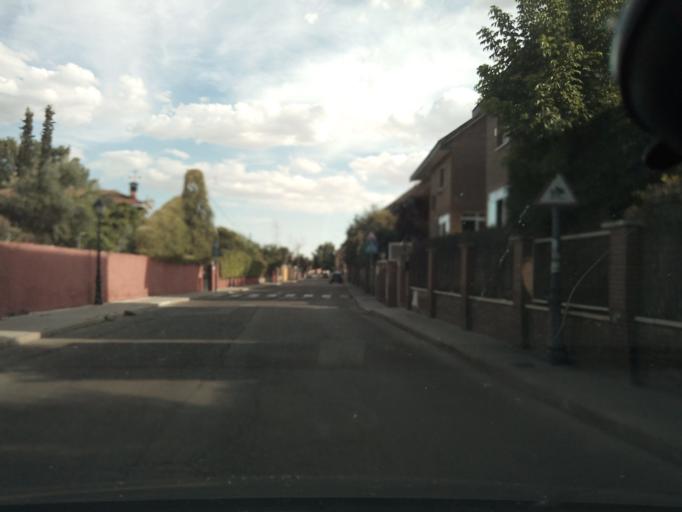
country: ES
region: Madrid
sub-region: Provincia de Madrid
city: Daganzo de Arriba
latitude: 40.5495
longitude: -3.4556
